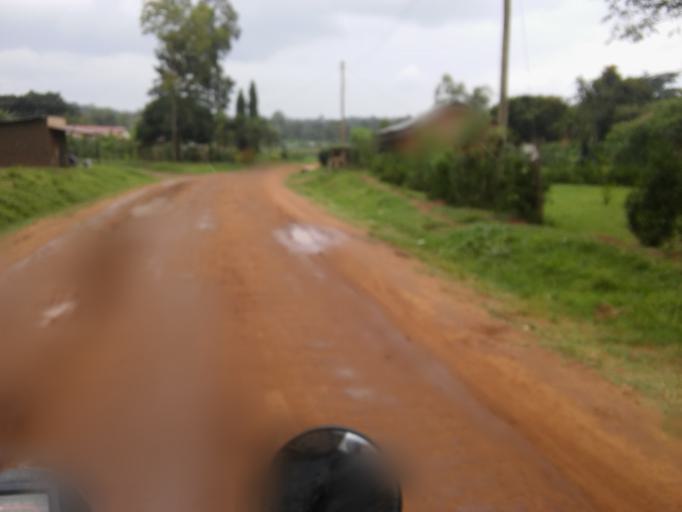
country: UG
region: Eastern Region
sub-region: Mbale District
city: Mbale
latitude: 1.0196
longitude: 34.1833
